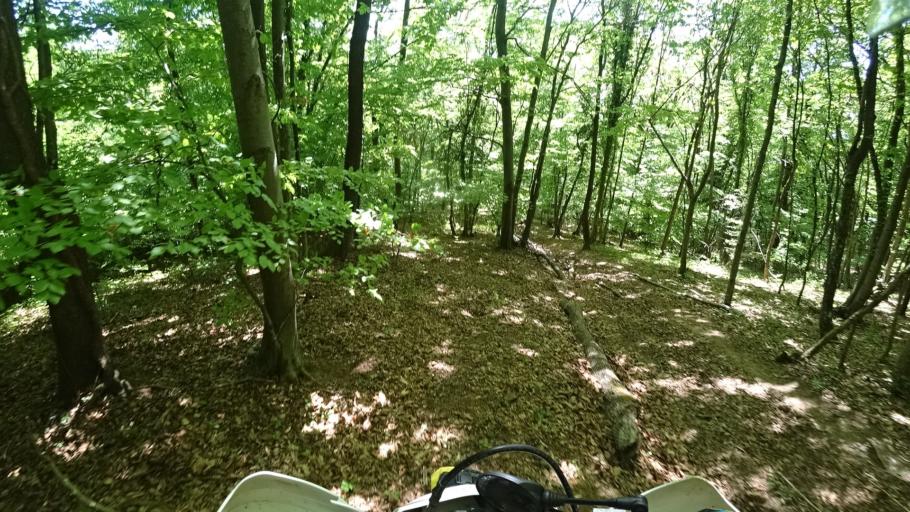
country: HR
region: Zagrebacka
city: Jablanovec
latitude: 45.8494
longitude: 15.8626
